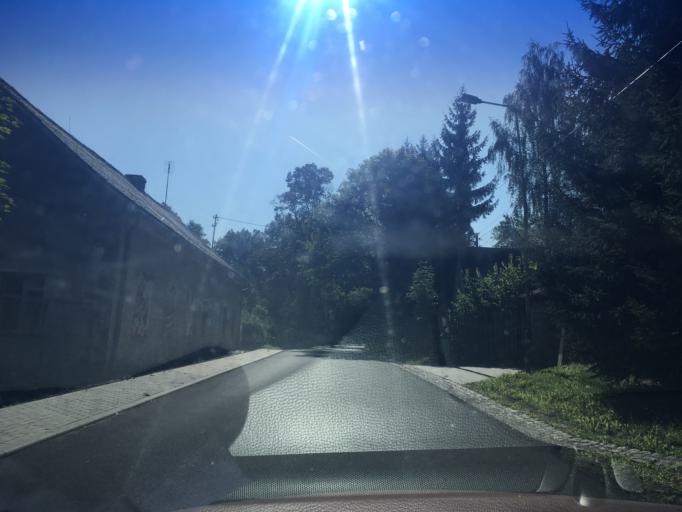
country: PL
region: Lower Silesian Voivodeship
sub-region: Powiat lubanski
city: Siekierczyn
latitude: 51.0491
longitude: 15.1665
